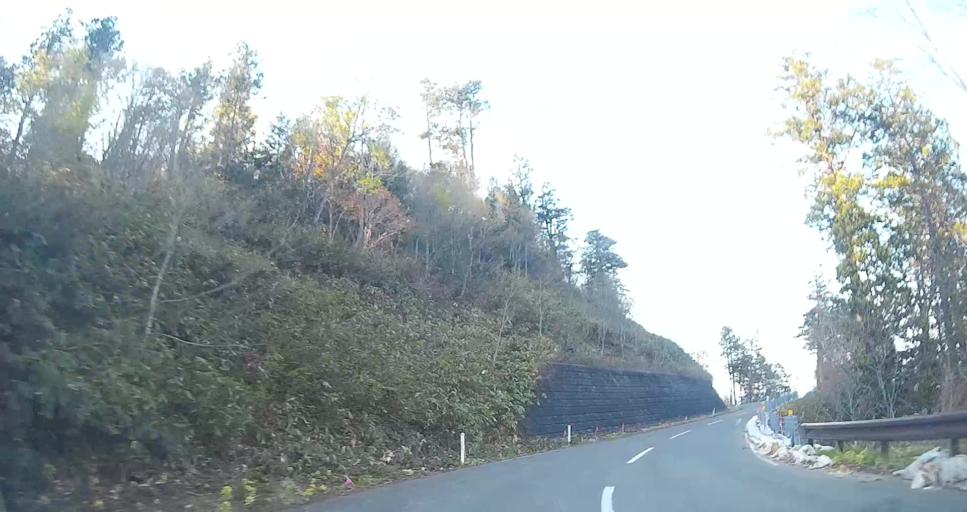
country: JP
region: Aomori
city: Mutsu
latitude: 41.3101
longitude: 141.1128
